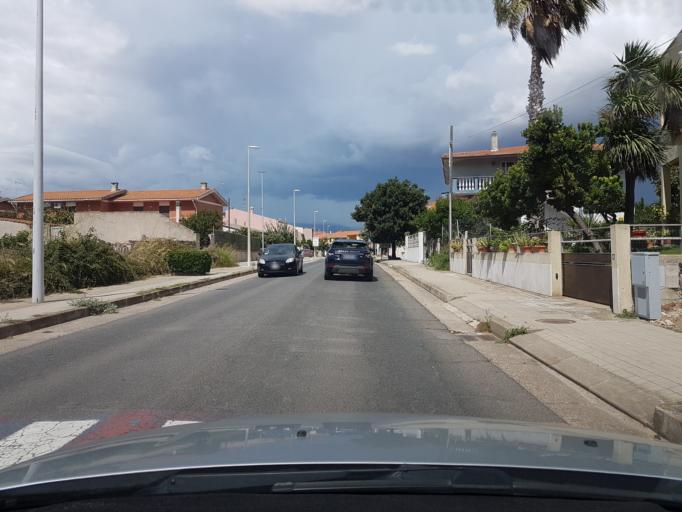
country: IT
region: Sardinia
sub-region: Provincia di Oristano
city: Riola Sardo
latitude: 39.9891
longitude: 8.5410
